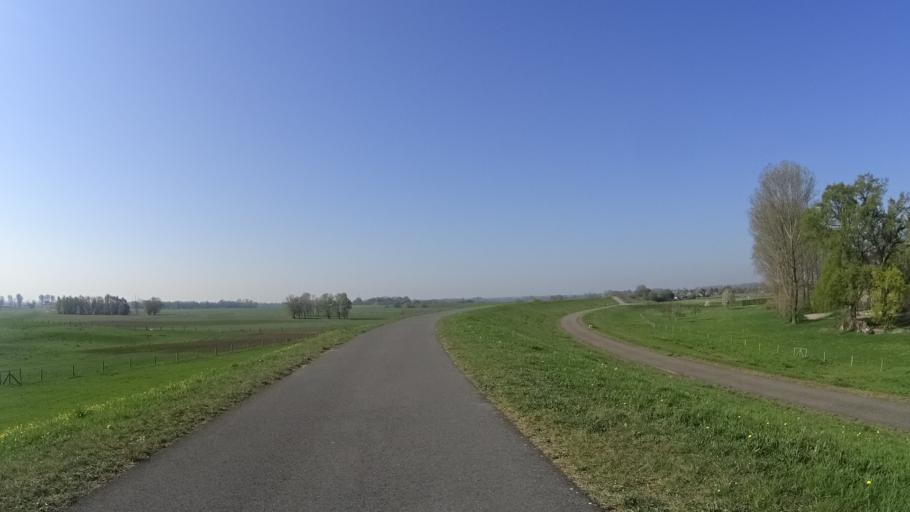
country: DE
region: North Rhine-Westphalia
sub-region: Regierungsbezirk Dusseldorf
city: Wesel
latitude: 51.6205
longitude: 6.5796
